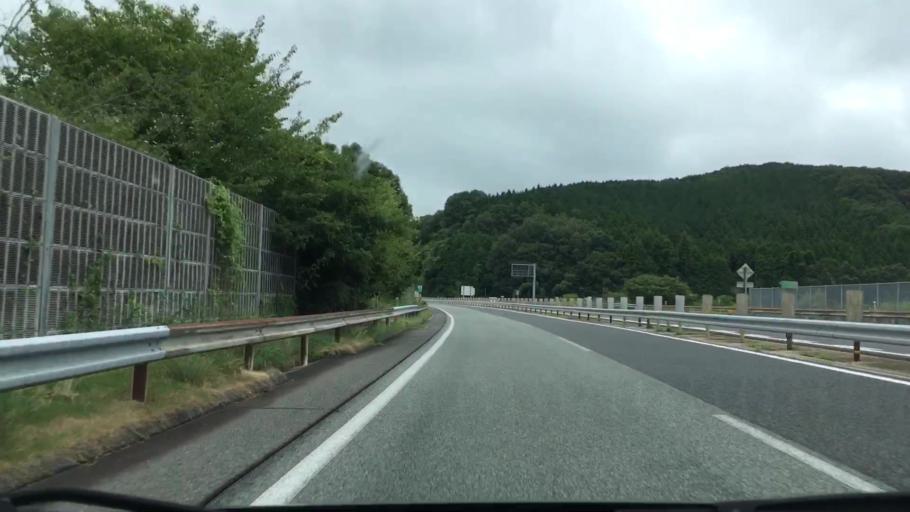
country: JP
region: Hiroshima
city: Miyoshi
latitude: 34.7886
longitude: 132.8520
